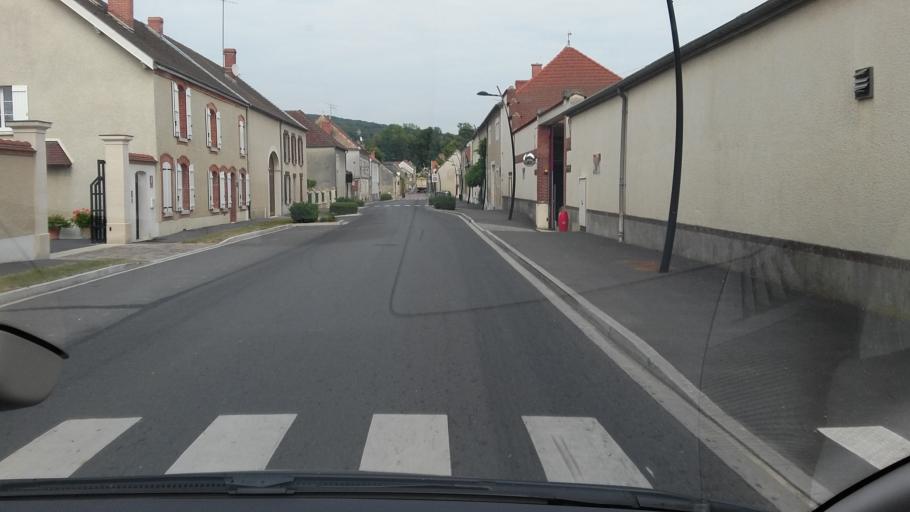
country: FR
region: Champagne-Ardenne
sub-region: Departement de la Marne
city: Tours-sur-Marne
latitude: 49.1003
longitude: 4.1130
